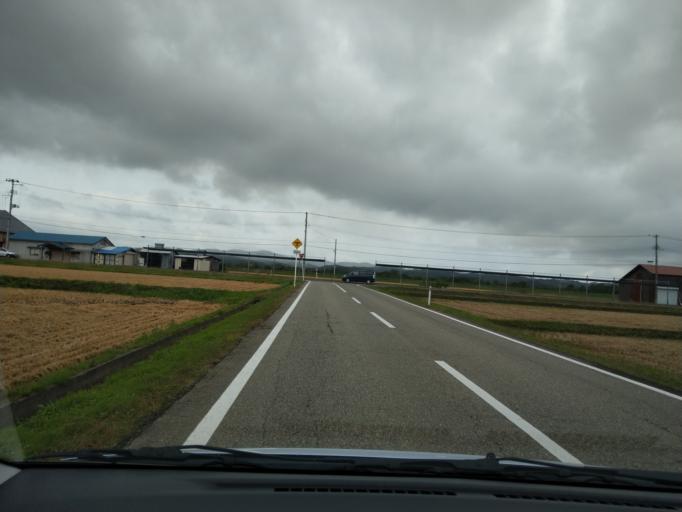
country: JP
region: Akita
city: Omagari
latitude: 39.3959
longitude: 140.4744
